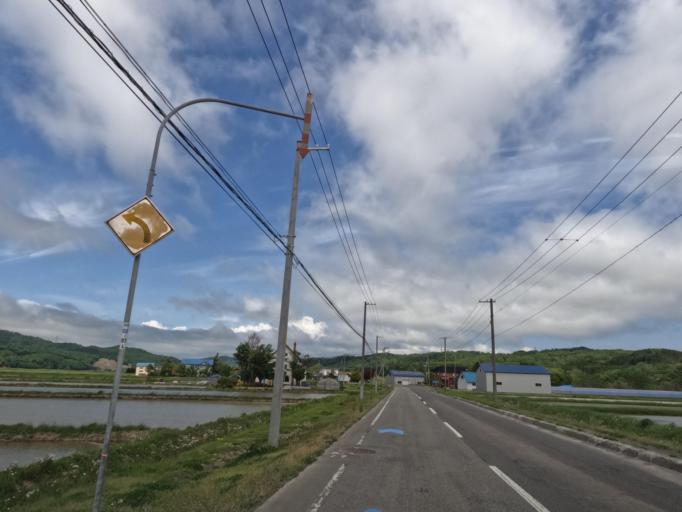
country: JP
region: Hokkaido
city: Tobetsu
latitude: 43.2737
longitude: 141.5327
